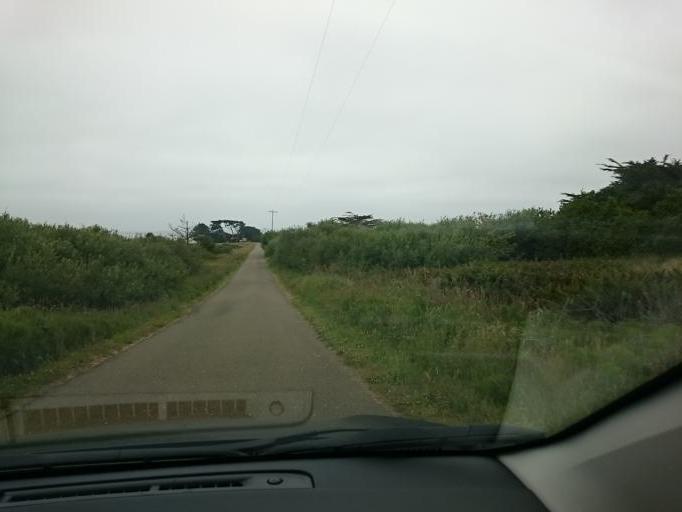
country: US
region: California
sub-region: Mendocino County
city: Fort Bragg
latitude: 39.3494
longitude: -123.8172
